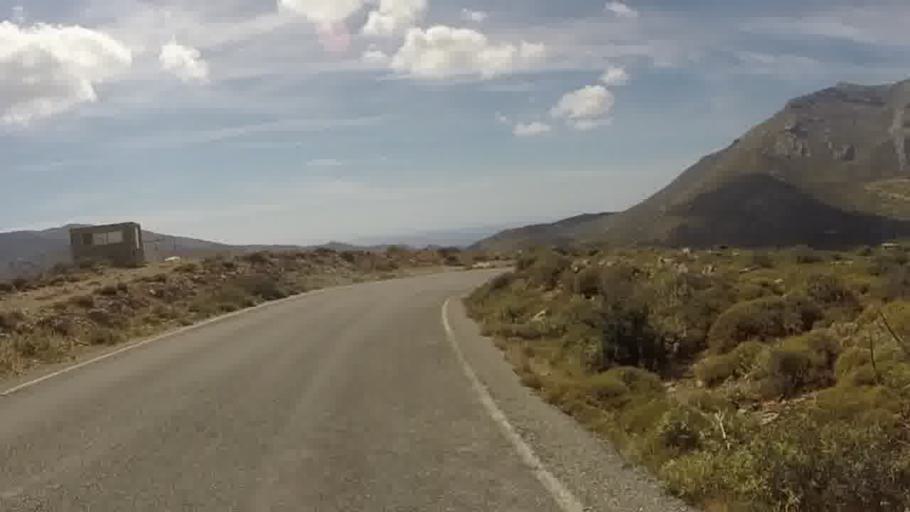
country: GR
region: Crete
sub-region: Nomos Rethymnis
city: Agia Galini
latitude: 35.1529
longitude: 24.6235
